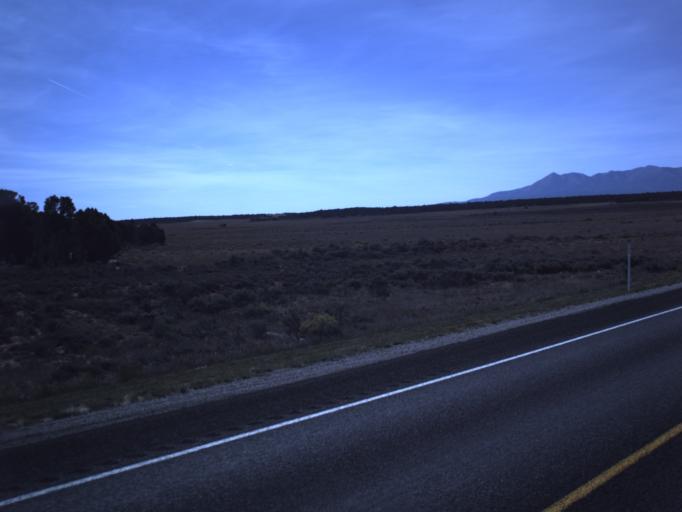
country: US
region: Colorado
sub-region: Dolores County
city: Dove Creek
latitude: 37.8317
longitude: -109.0949
